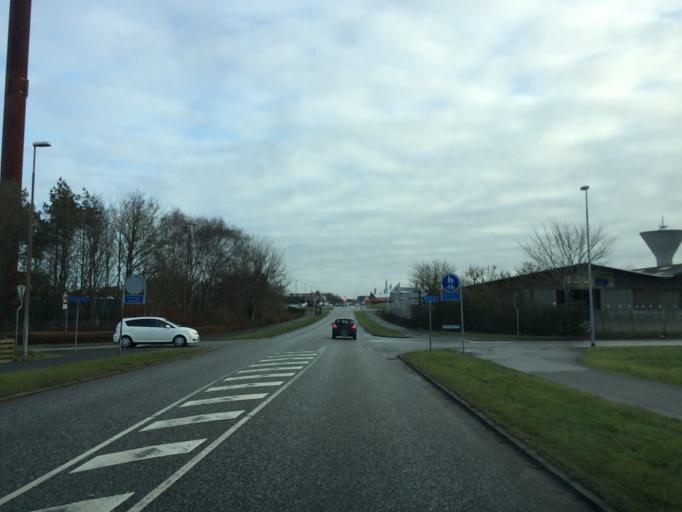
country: DK
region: Central Jutland
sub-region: Struer Kommune
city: Struer
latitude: 56.4886
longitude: 8.5791
